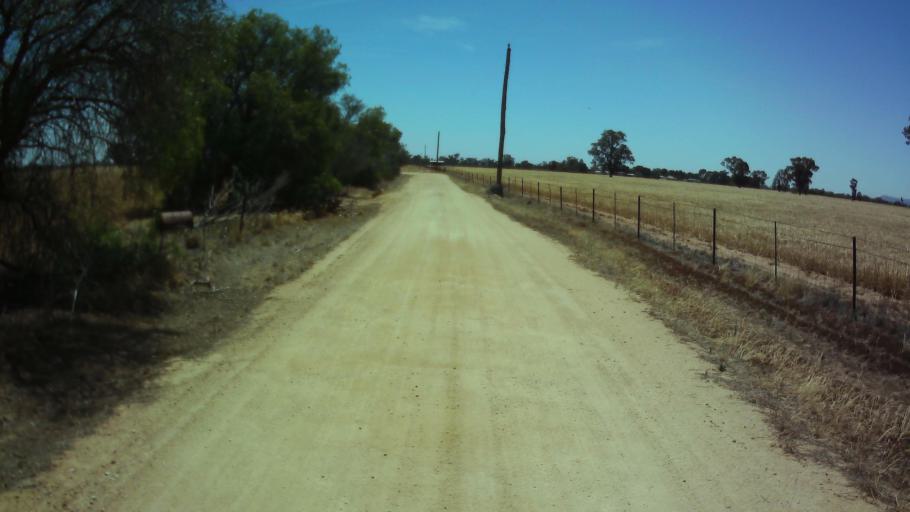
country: AU
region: New South Wales
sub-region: Weddin
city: Grenfell
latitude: -34.0566
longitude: 147.7754
